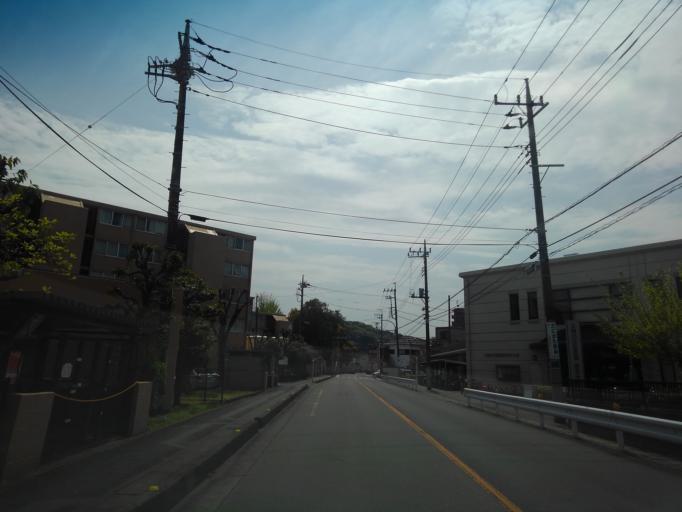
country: JP
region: Saitama
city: Hanno
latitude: 35.8399
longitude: 139.3618
